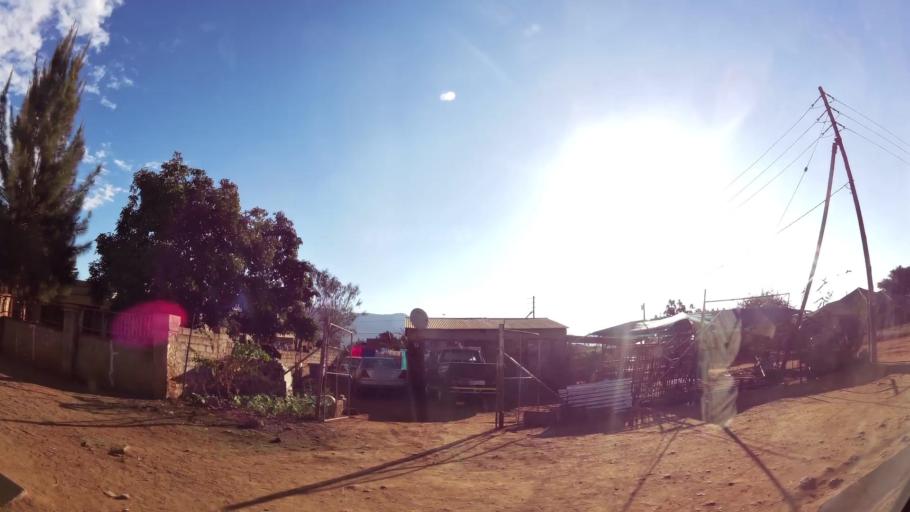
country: ZA
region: Limpopo
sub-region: Waterberg District Municipality
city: Mokopane
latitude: -24.1812
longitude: 28.9831
